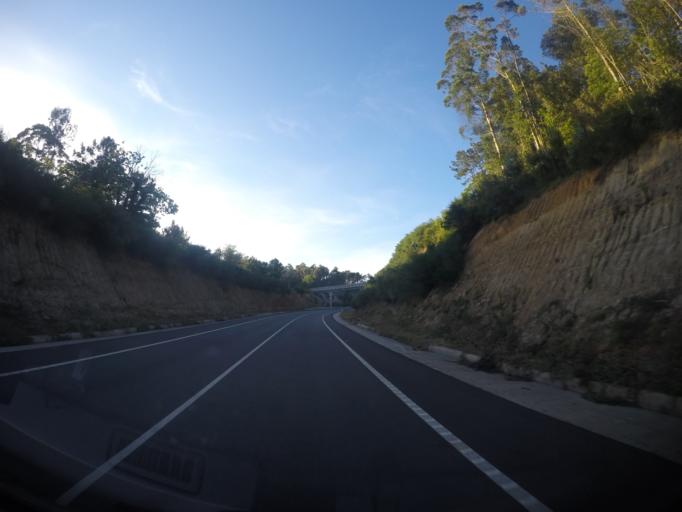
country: ES
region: Galicia
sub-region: Provincia da Coruna
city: Noia
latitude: 42.8087
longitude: -8.8891
